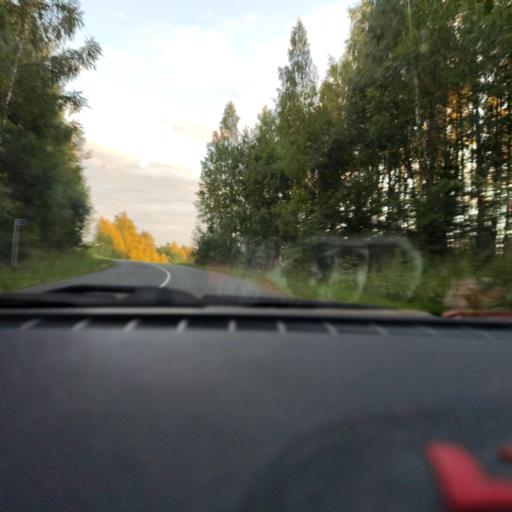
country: RU
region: Perm
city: Ocher
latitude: 57.9323
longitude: 54.7881
